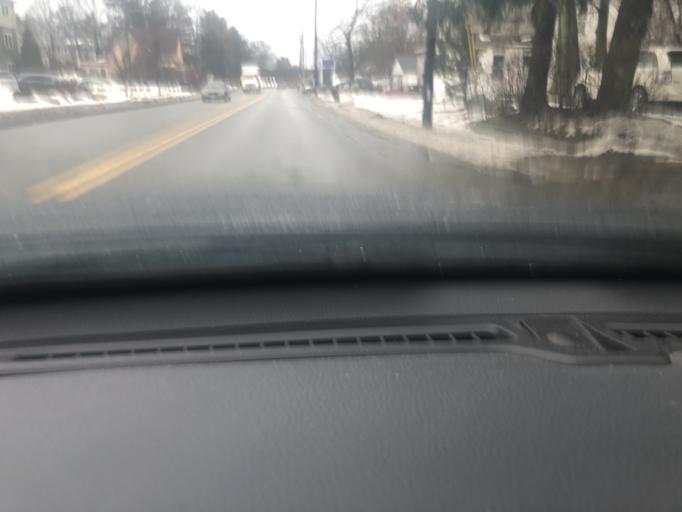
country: US
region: Massachusetts
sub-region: Norfolk County
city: Avon
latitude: 42.1007
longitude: -71.0602
